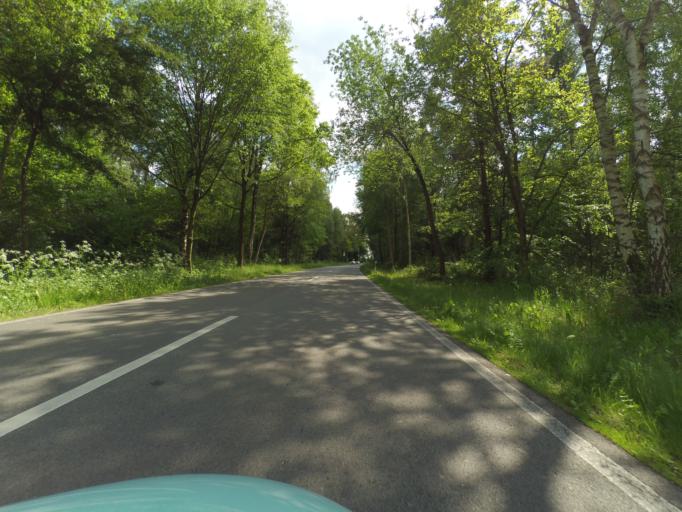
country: DE
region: Lower Saxony
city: Nienhagen
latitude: 52.5253
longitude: 10.0870
